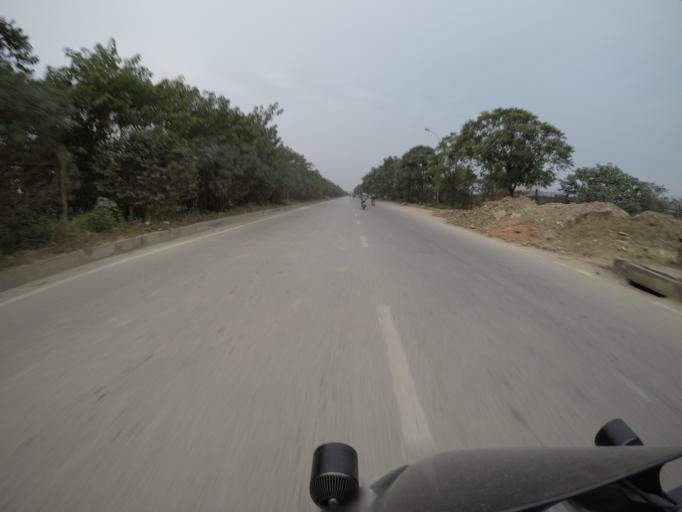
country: VN
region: Ha Noi
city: Cau Dien
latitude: 21.0082
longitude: 105.7564
